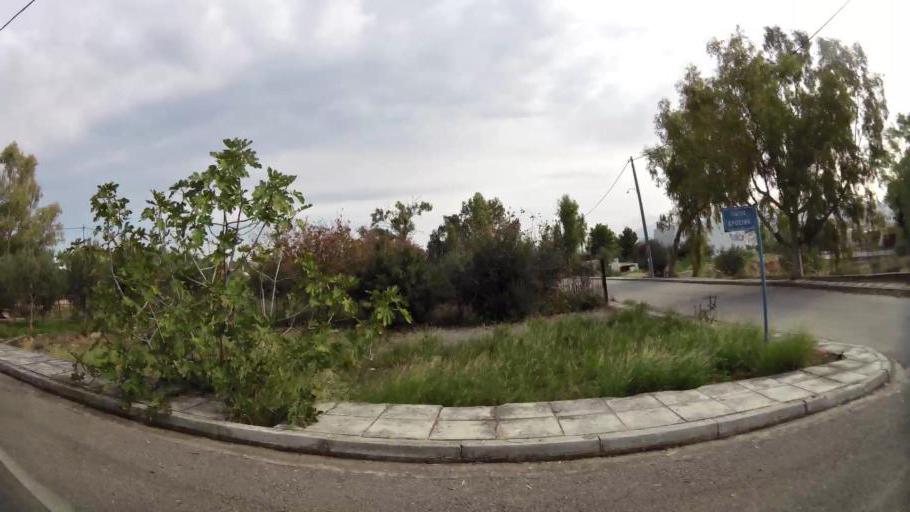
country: GR
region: Attica
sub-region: Nomarchia Athinas
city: Kamateron
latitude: 38.0555
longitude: 23.7025
